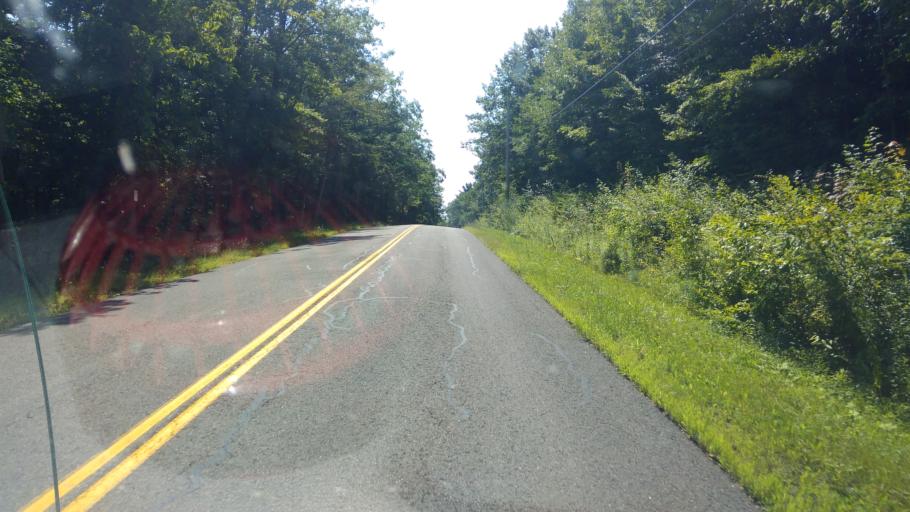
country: US
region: New York
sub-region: Allegany County
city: Belmont
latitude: 42.2877
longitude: -77.9958
